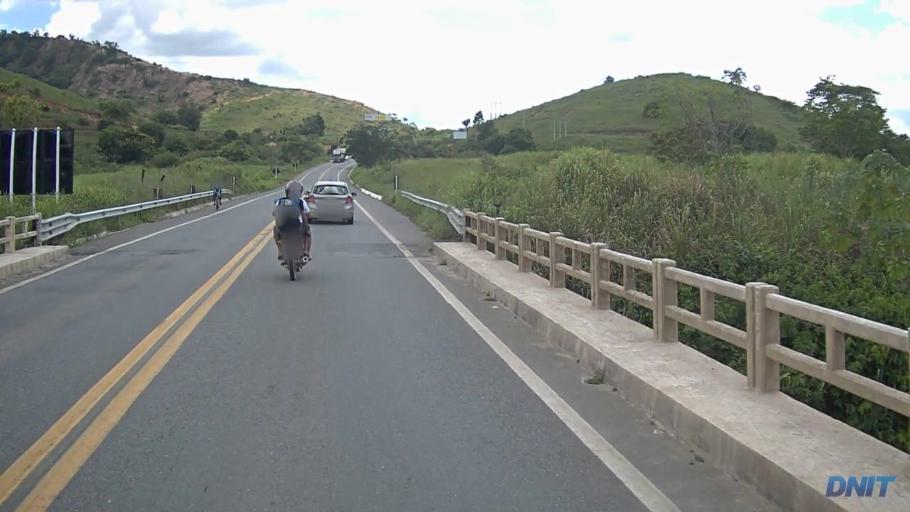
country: BR
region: Minas Gerais
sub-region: Governador Valadares
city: Governador Valadares
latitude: -18.9460
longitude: -42.0666
